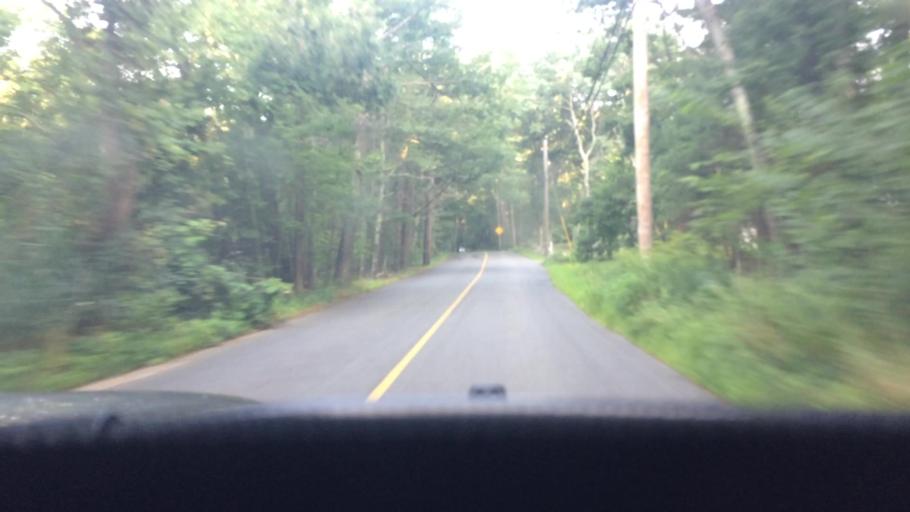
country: US
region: Massachusetts
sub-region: Middlesex County
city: North Reading
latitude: 42.6118
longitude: -71.0957
